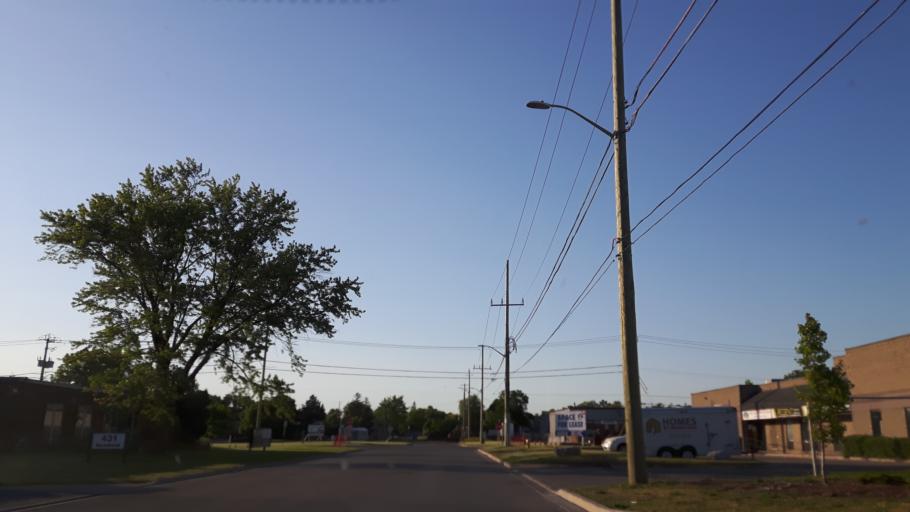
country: CA
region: Ontario
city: London
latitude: 42.9331
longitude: -81.2122
